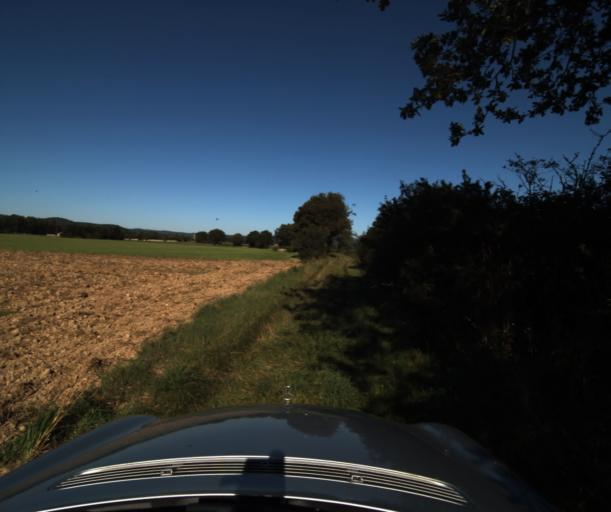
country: FR
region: Midi-Pyrenees
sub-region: Departement de l'Ariege
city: Lavelanet
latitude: 42.9853
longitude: 1.8941
